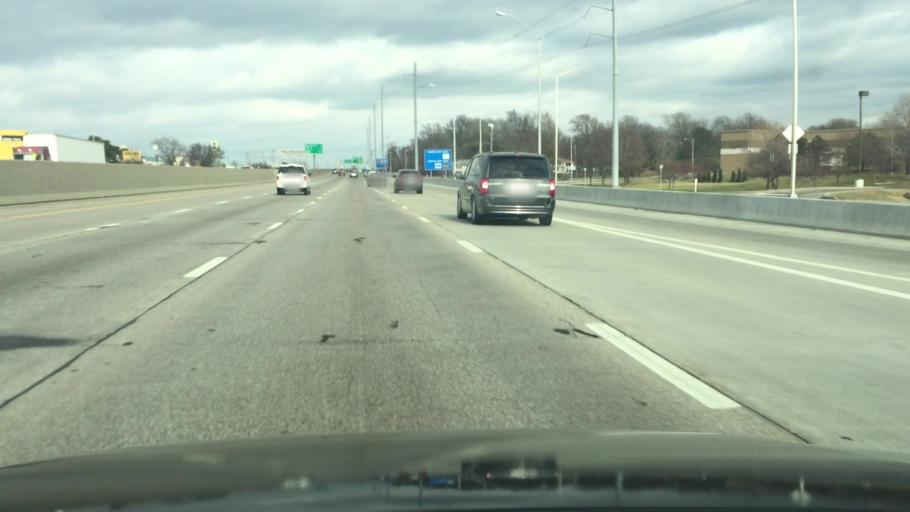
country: US
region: Kansas
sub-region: Johnson County
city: Lenexa
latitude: 38.9584
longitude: -94.7305
